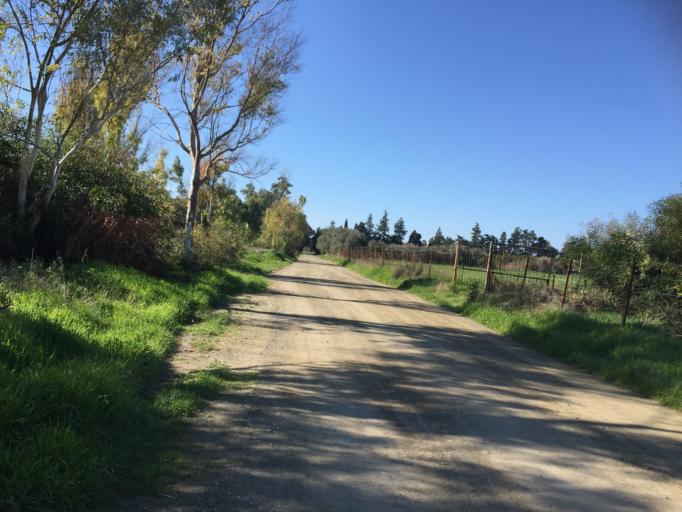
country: CY
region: Larnaka
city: Kolossi
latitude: 34.6341
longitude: 32.9666
